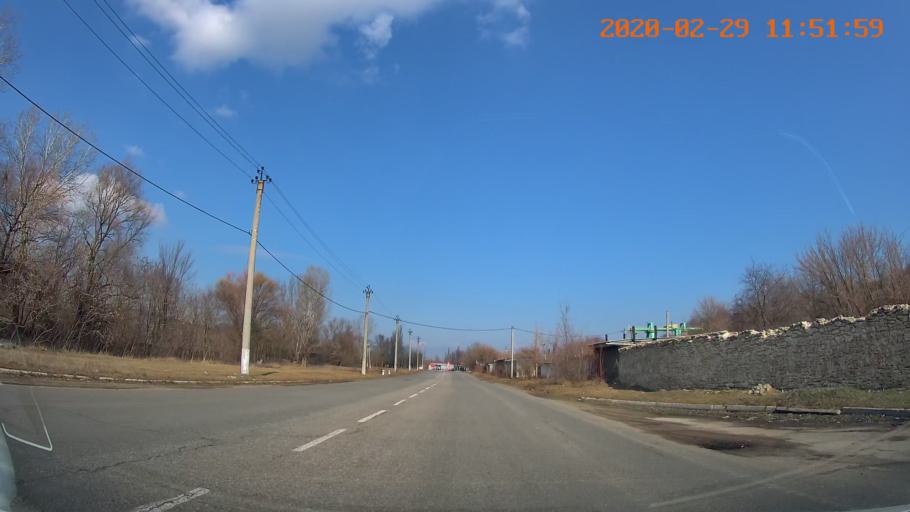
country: MD
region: Telenesti
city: Ribnita
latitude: 47.7684
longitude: 28.9912
